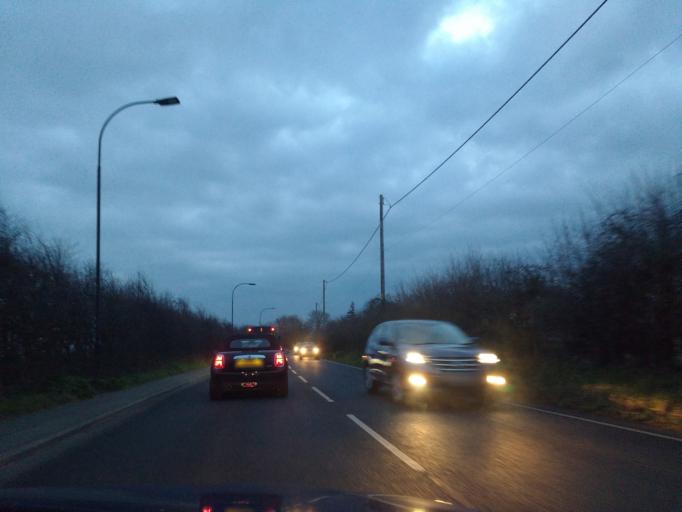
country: GB
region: England
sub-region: Isle of Wight
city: Northwood
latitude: 50.7336
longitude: -1.3063
